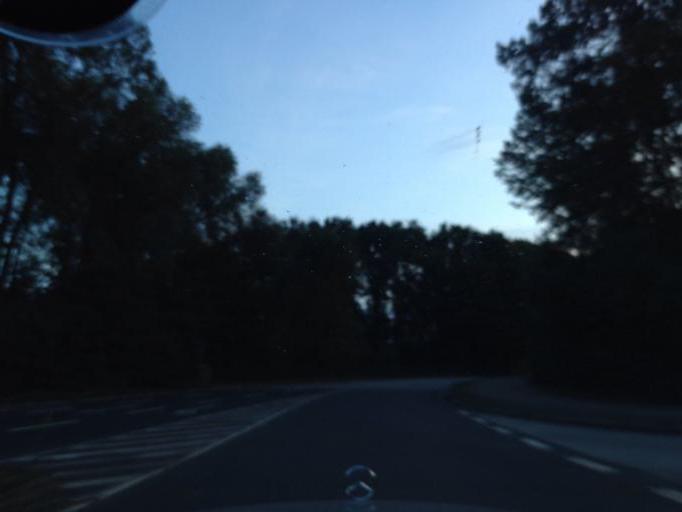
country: DE
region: Schleswig-Holstein
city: Delingsdorf
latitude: 53.6774
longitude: 10.2493
